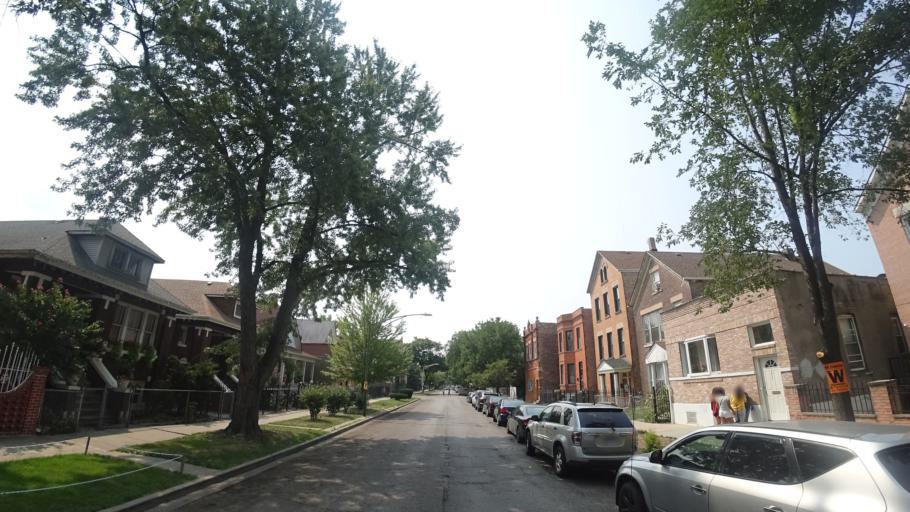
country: US
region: Illinois
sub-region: Cook County
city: Cicero
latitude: 41.8432
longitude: -87.7197
